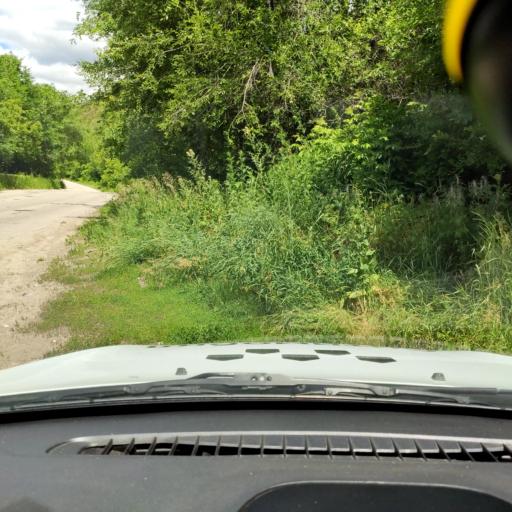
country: RU
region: Samara
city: Zhigulevsk
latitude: 53.3990
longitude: 49.4131
